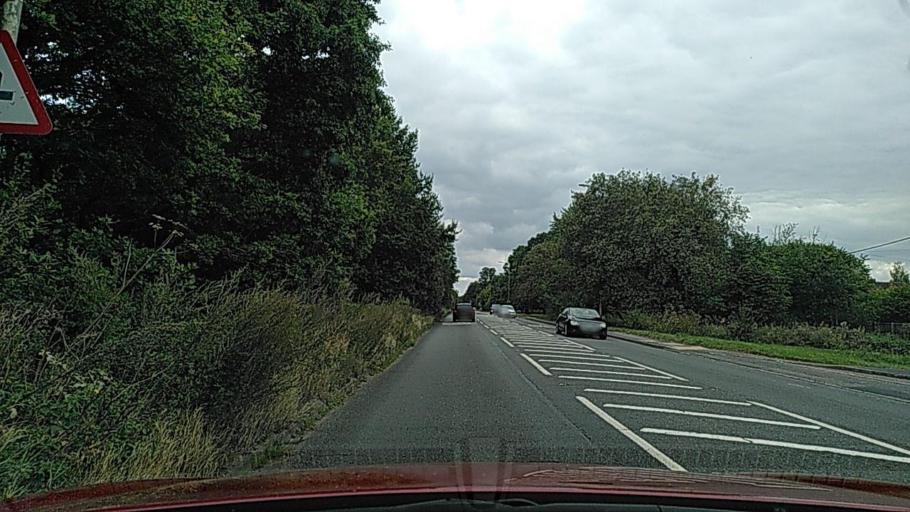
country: GB
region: England
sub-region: Royal Borough of Windsor and Maidenhead
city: White Waltham
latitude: 51.5151
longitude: -0.7971
